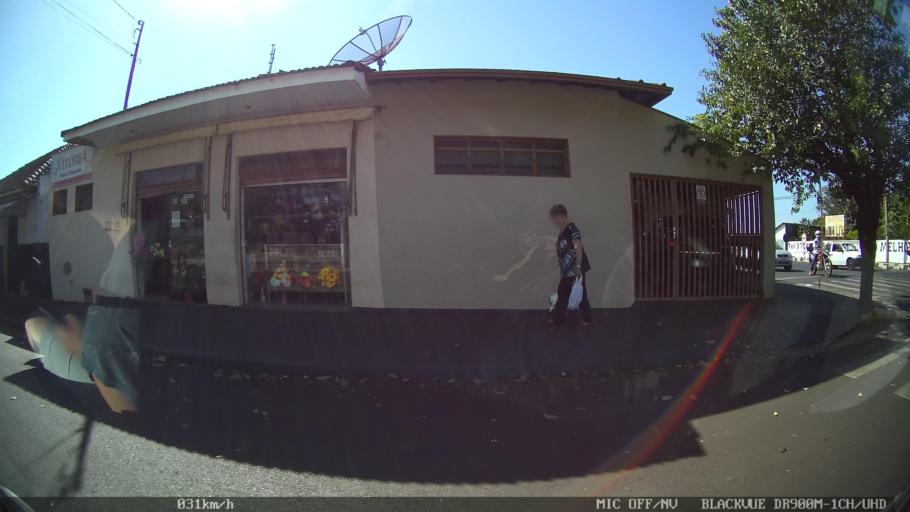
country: BR
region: Sao Paulo
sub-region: Batatais
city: Batatais
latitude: -20.8992
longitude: -47.5835
